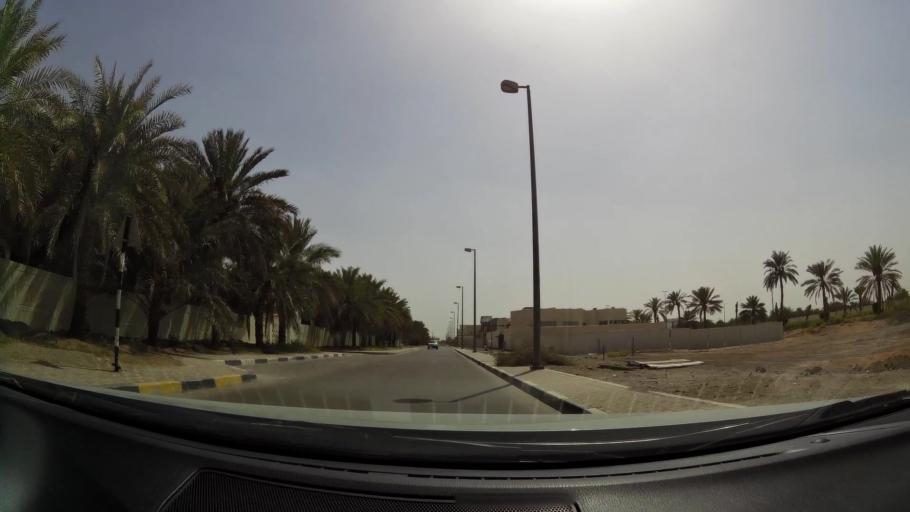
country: AE
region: Abu Dhabi
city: Al Ain
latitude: 24.2255
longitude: 55.6877
